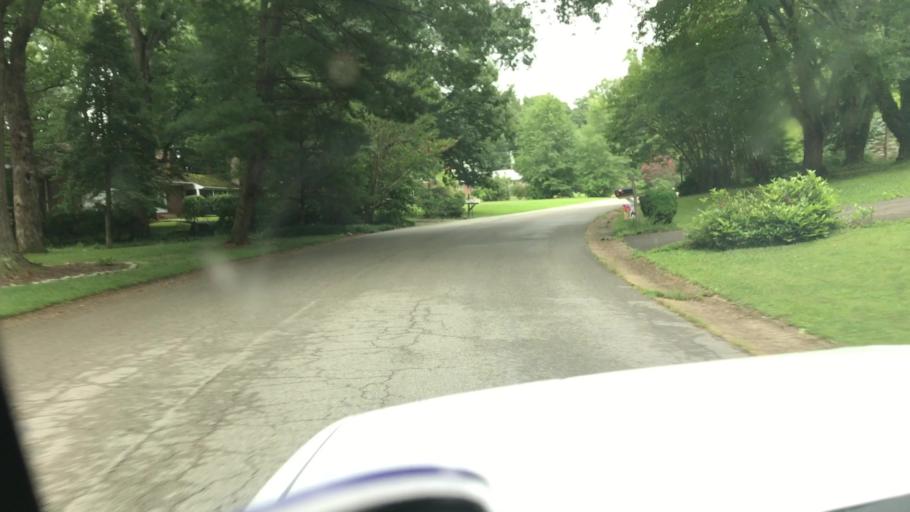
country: US
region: Virginia
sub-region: Henrico County
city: Short Pump
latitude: 37.6045
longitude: -77.7132
